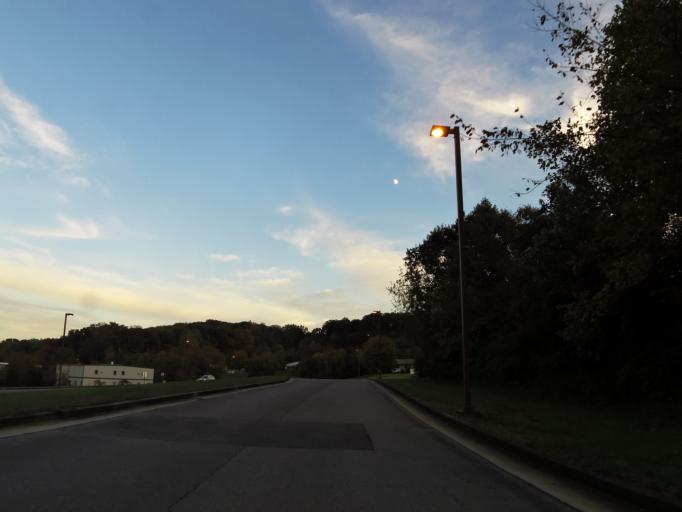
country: US
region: Tennessee
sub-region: Blount County
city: Eagleton Village
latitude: 35.8621
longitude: -83.9395
